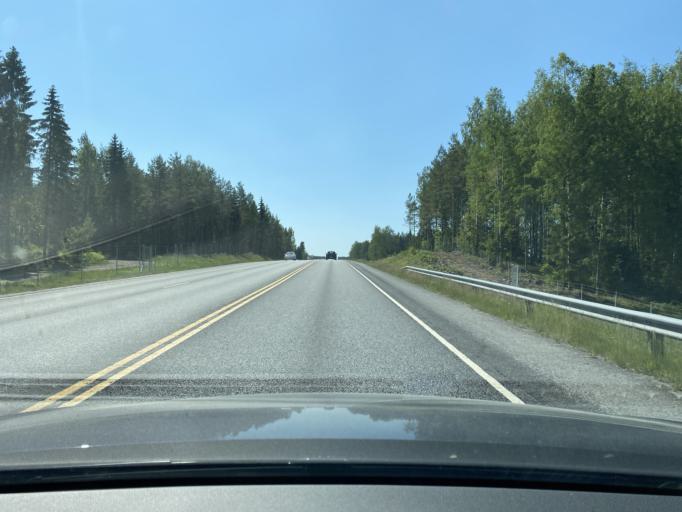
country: FI
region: Pirkanmaa
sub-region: Tampere
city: Nokia
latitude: 61.4033
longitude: 23.2741
